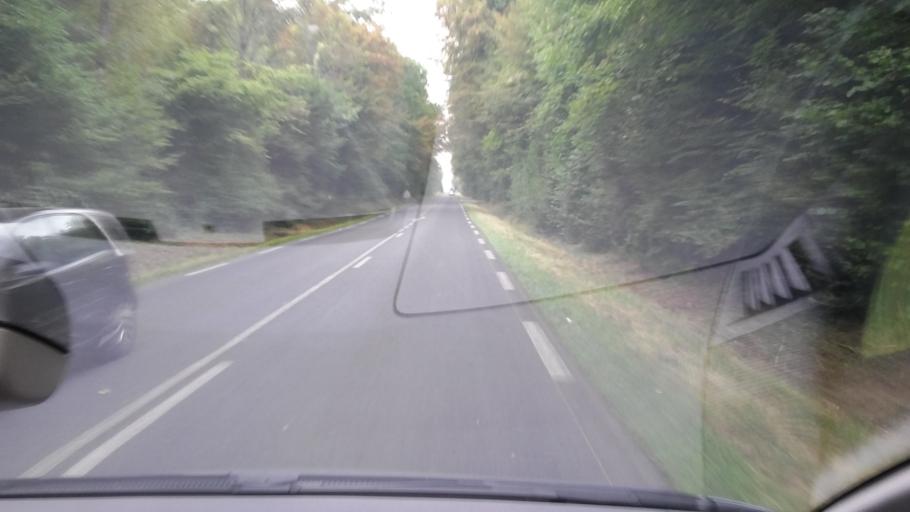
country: FR
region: Champagne-Ardenne
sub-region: Departement de la Marne
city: Verzenay
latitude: 49.1411
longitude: 4.1029
